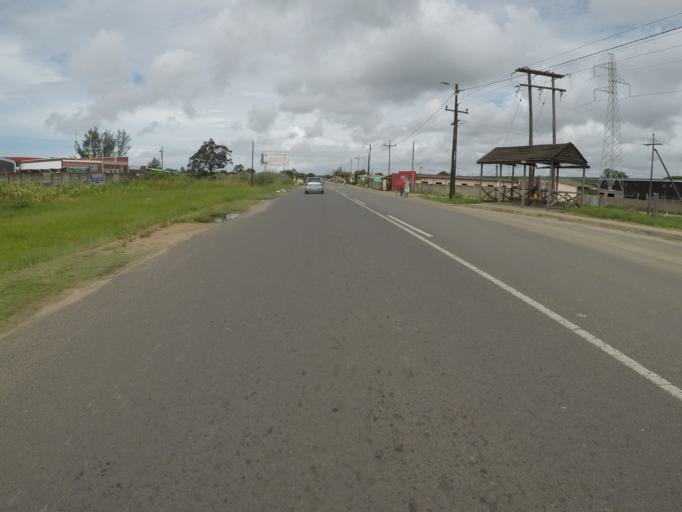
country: ZA
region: KwaZulu-Natal
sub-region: uThungulu District Municipality
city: eSikhawini
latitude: -28.8673
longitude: 31.9062
